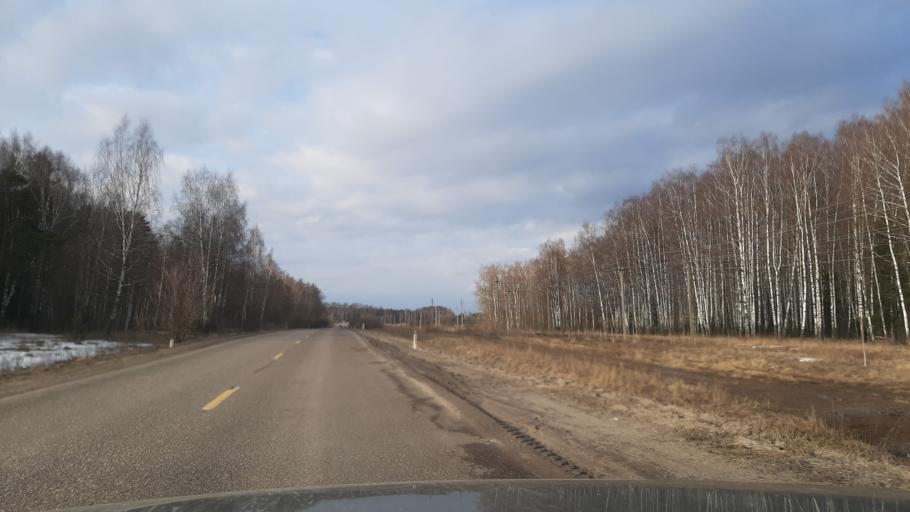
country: RU
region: Ivanovo
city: Novo-Talitsy
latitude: 56.9272
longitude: 40.7365
